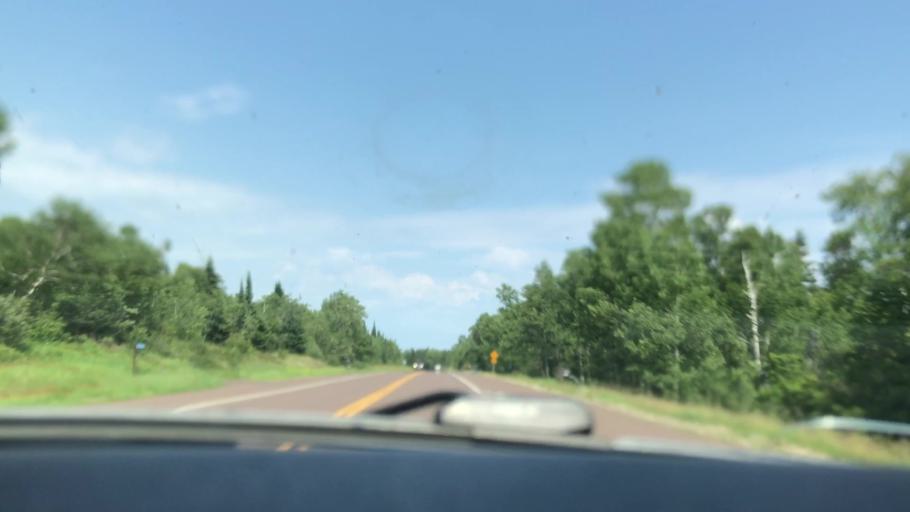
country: US
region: Minnesota
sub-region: Cook County
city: Grand Marais
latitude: 47.7766
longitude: -90.1988
